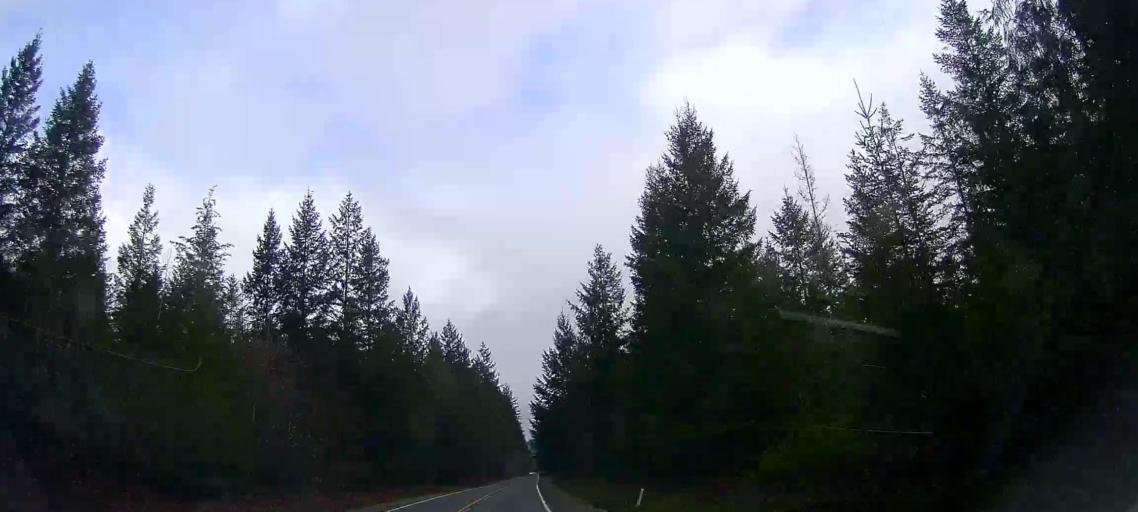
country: US
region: Washington
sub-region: Snohomish County
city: Darrington
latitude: 48.5254
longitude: -121.8344
